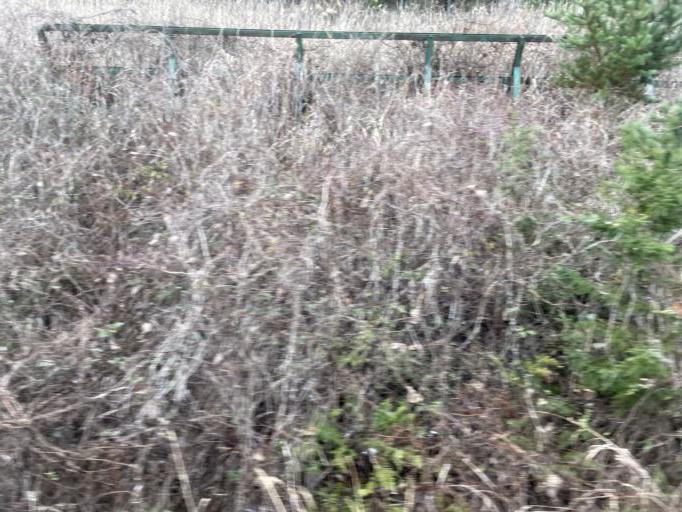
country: JP
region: Aomori
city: Aomori Shi
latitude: 41.0314
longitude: 140.6461
